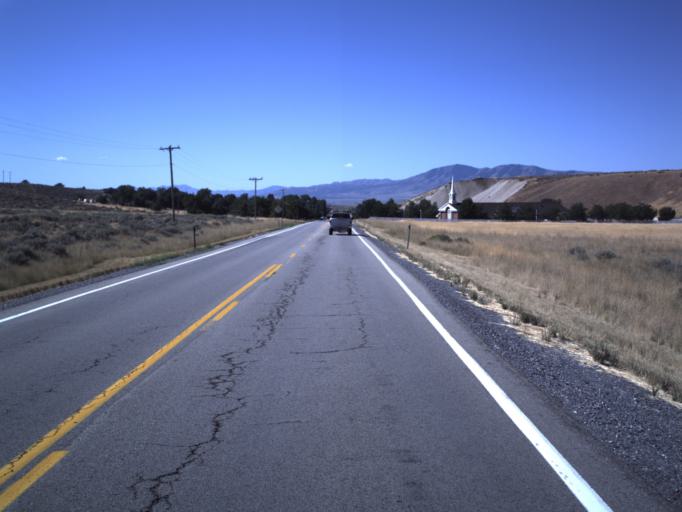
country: US
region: Utah
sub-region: Tooele County
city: Tooele
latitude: 40.4610
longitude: -112.3564
